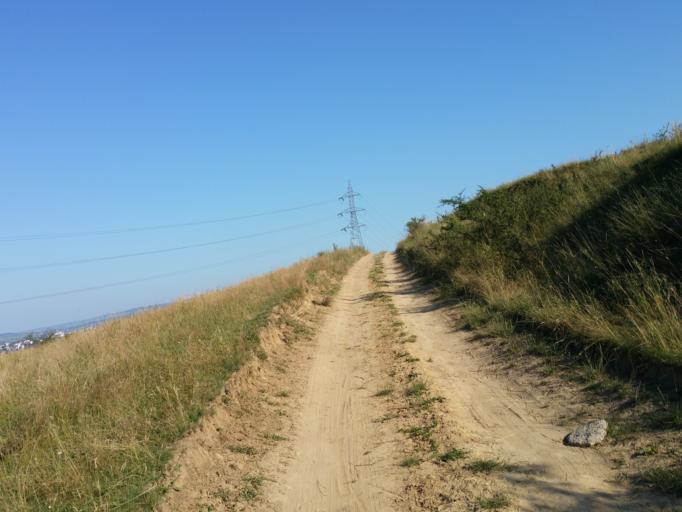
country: RO
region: Cluj
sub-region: Comuna Baciu
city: Baciu
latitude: 46.7969
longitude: 23.5297
